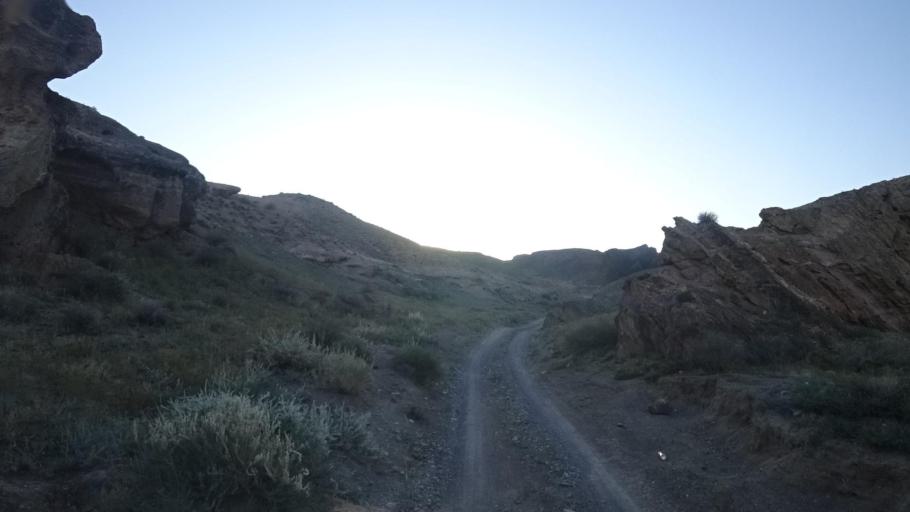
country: KZ
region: Almaty Oblysy
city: Kegen
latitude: 43.2722
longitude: 78.9761
